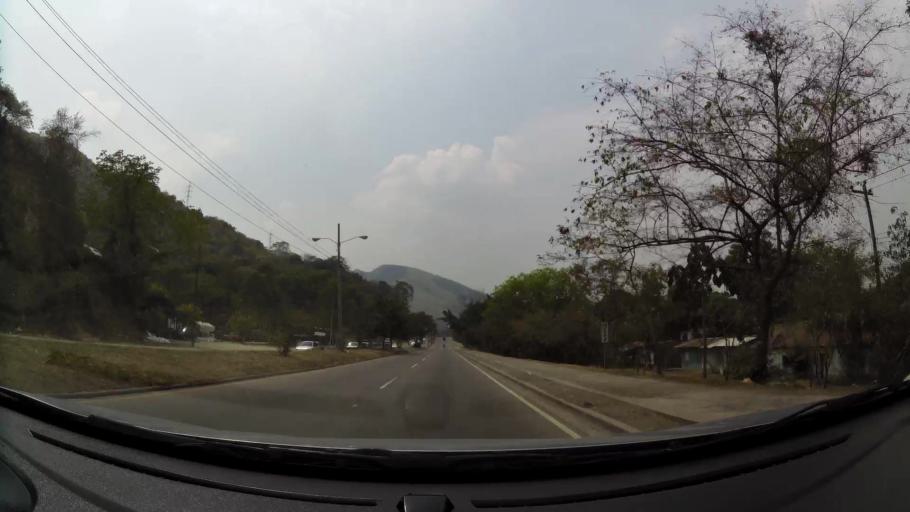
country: HN
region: Cortes
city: Chotepe
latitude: 15.4189
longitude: -88.0174
